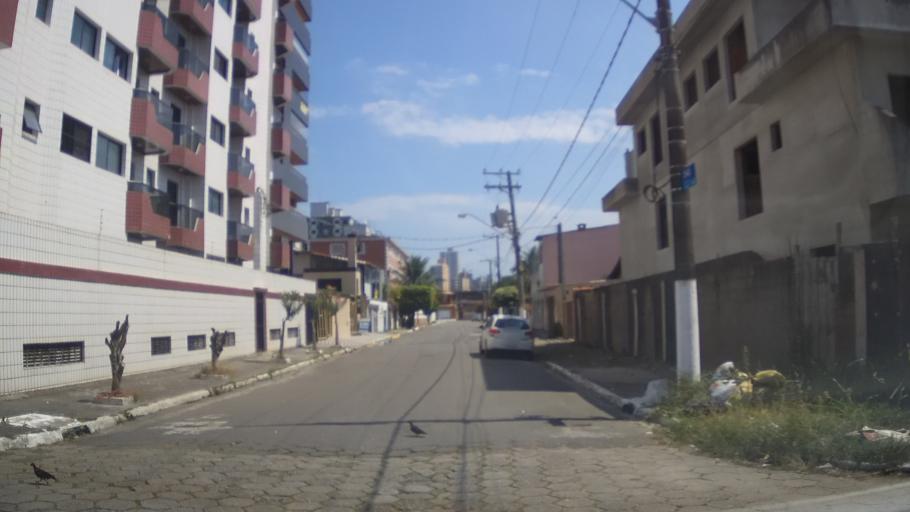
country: BR
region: Sao Paulo
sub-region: Praia Grande
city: Praia Grande
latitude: -24.0115
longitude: -46.4315
